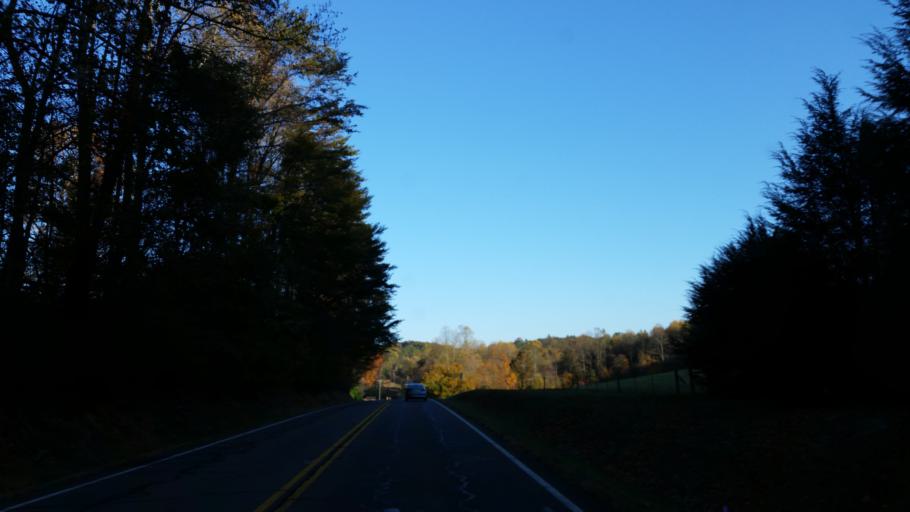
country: US
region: Georgia
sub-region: Pickens County
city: Jasper
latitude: 34.6020
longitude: -84.3429
